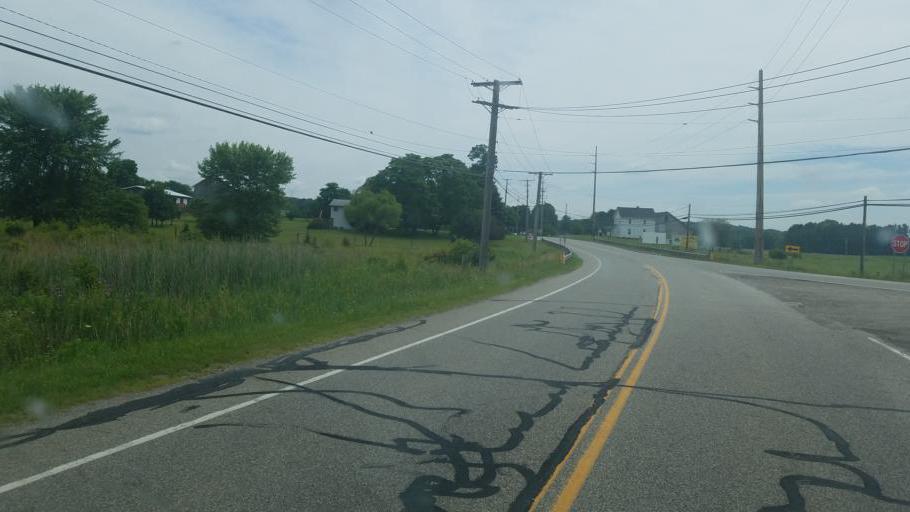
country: US
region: Ohio
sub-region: Geauga County
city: Bainbridge
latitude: 41.3885
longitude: -81.2796
